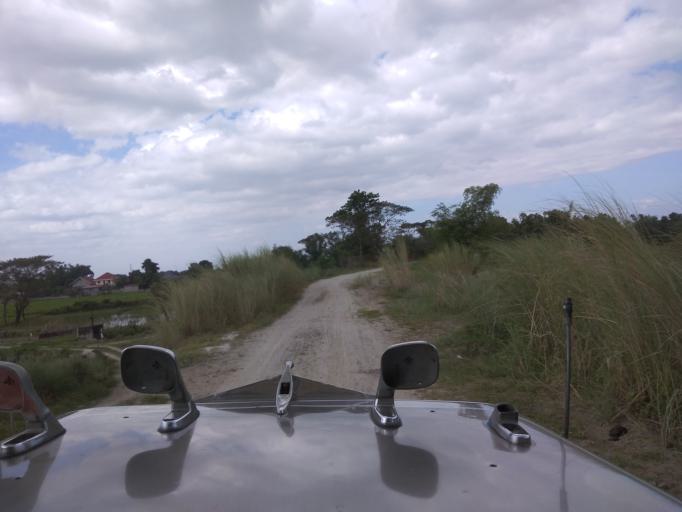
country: PH
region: Central Luzon
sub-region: Province of Pampanga
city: San Patricio
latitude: 15.1141
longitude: 120.7139
